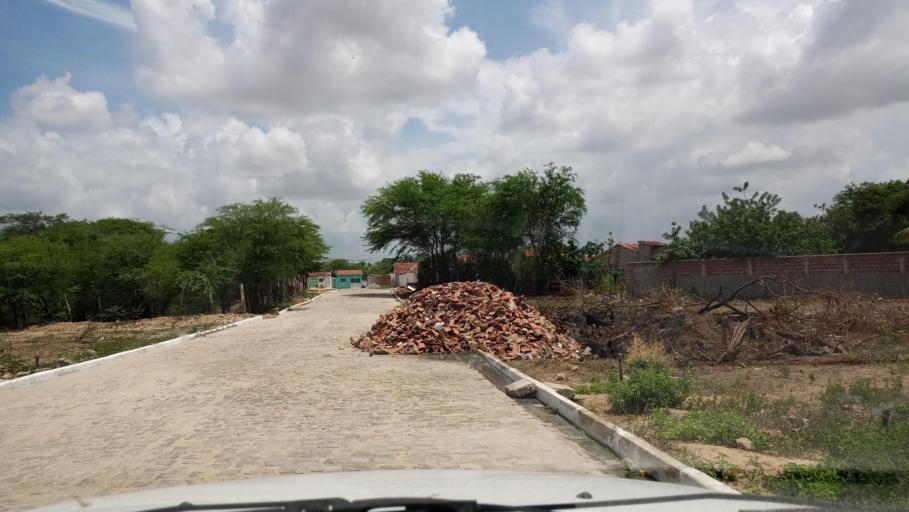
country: BR
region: Rio Grande do Norte
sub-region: Tangara
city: Tangara
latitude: -6.1050
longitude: -35.7145
